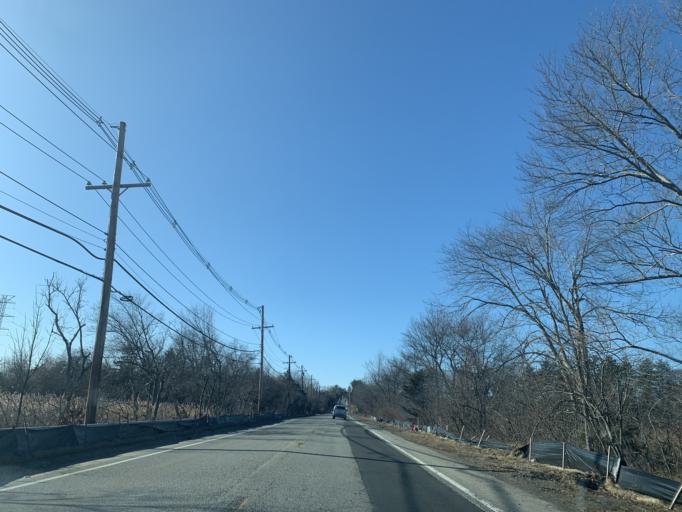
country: US
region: Massachusetts
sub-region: Middlesex County
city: Wayland
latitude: 42.3632
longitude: -71.3769
